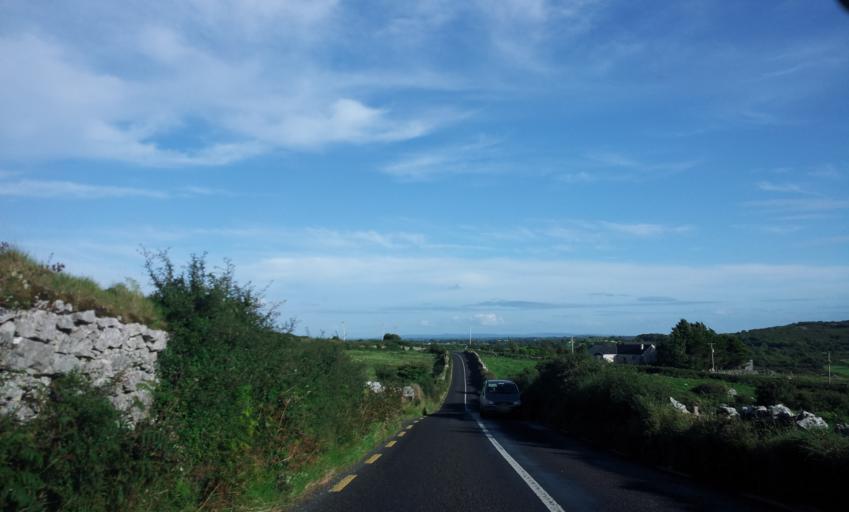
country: IE
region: Munster
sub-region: An Clar
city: Ennis
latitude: 52.9794
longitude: -9.1184
